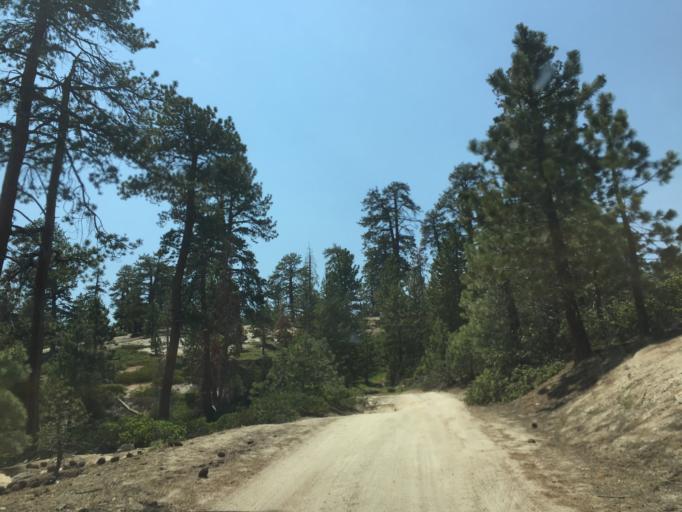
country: US
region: California
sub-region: Tulare County
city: Three Rivers
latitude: 36.7251
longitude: -118.8579
